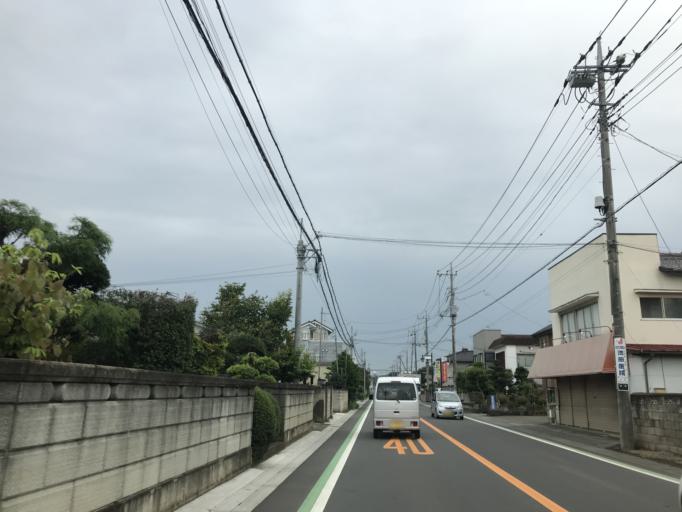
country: JP
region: Ibaraki
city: Sakai
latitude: 36.1025
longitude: 139.8018
